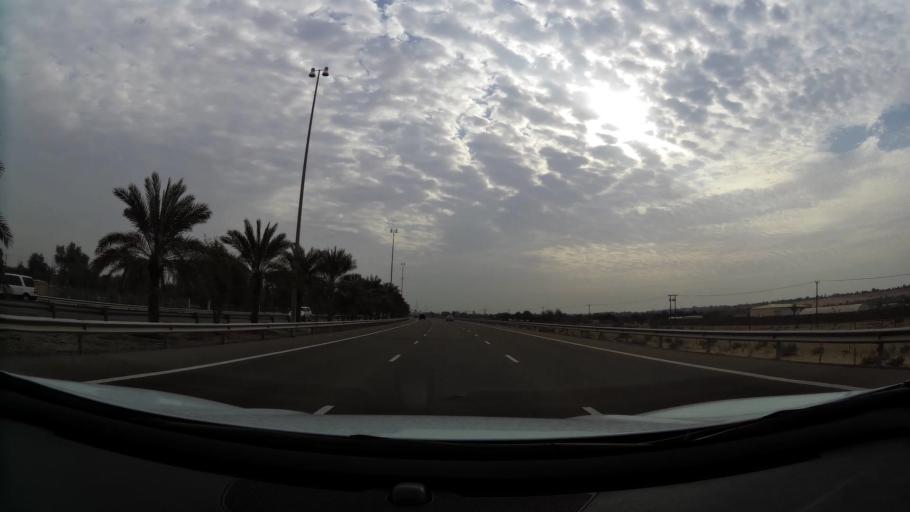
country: AE
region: Abu Dhabi
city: Al Ain
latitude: 24.1685
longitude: 55.0878
